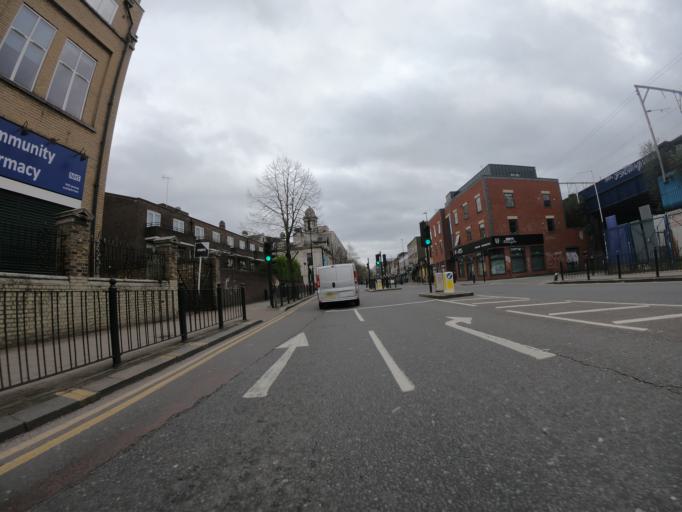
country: GB
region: England
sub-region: Greater London
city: Bethnal Green
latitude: 51.5309
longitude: -0.0564
